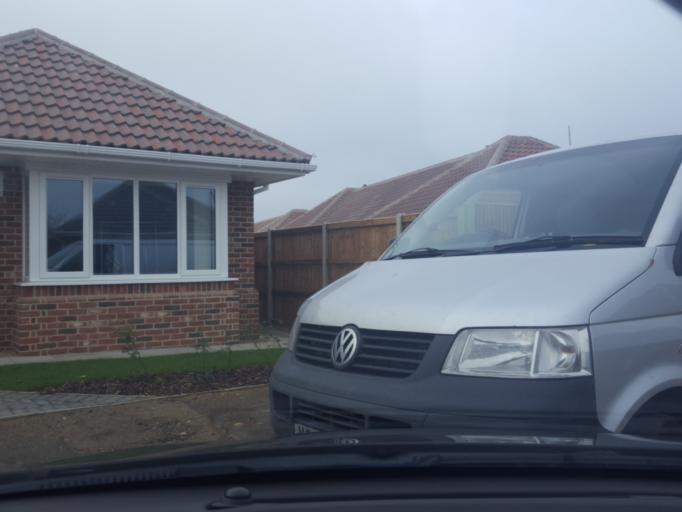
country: GB
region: England
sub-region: Essex
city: Clacton-on-Sea
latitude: 51.8004
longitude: 1.1752
